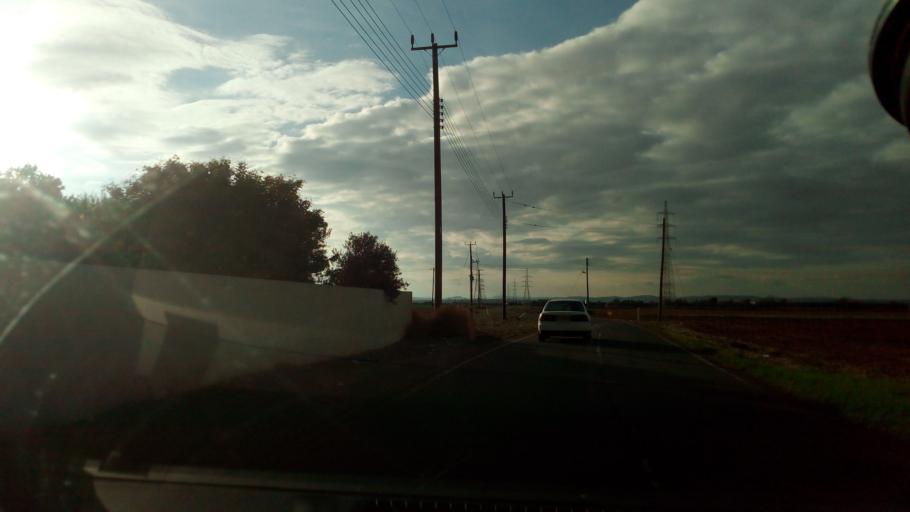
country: CY
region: Larnaka
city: Xylotymbou
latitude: 35.0011
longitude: 33.7926
